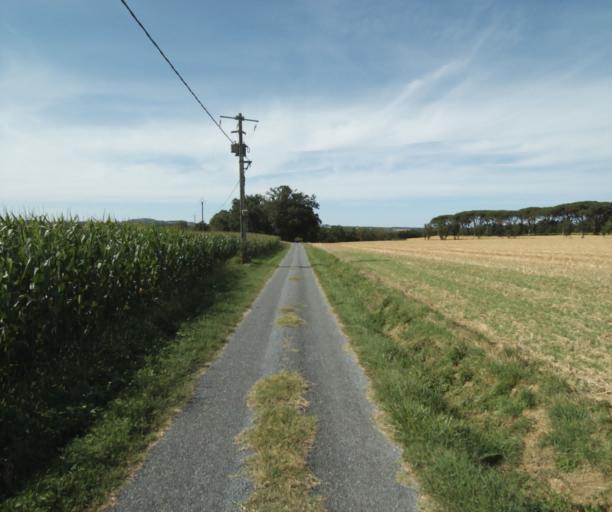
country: FR
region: Midi-Pyrenees
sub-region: Departement du Tarn
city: Soual
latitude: 43.5171
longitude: 2.0874
